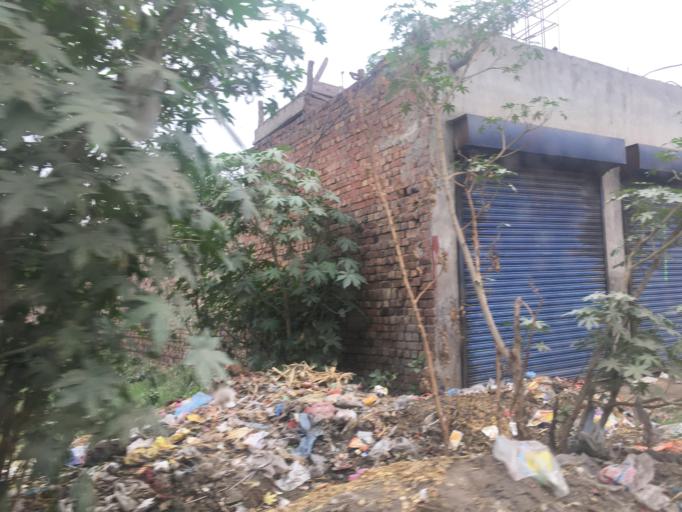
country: PK
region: Punjab
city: Lahore
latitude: 31.6165
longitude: 74.3675
